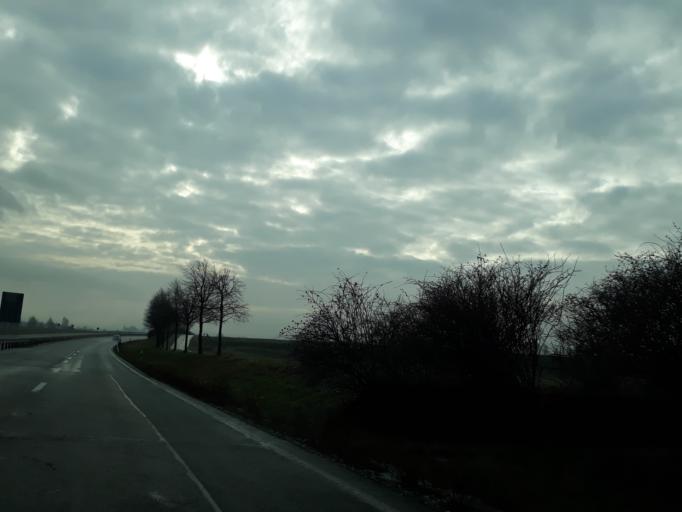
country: DE
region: Saxony
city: Lobau
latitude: 51.1082
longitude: 14.6489
